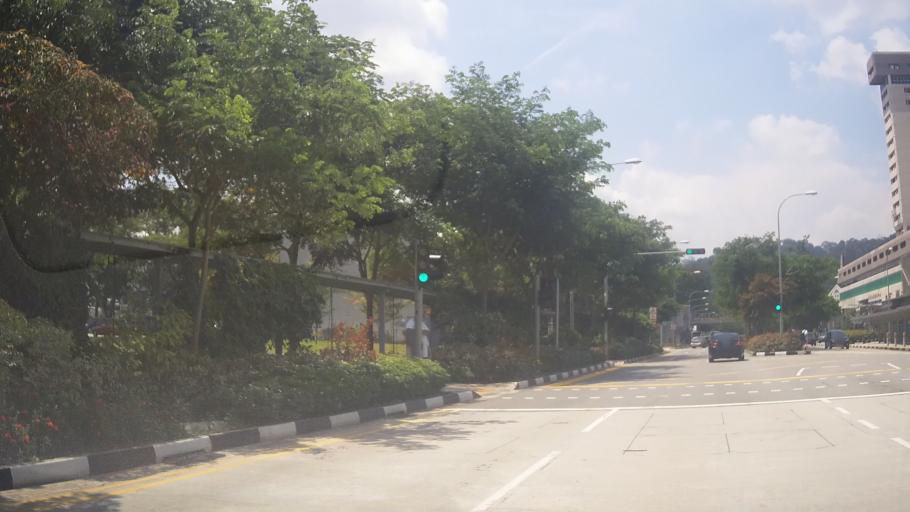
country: SG
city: Singapore
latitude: 1.3411
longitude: 103.7758
